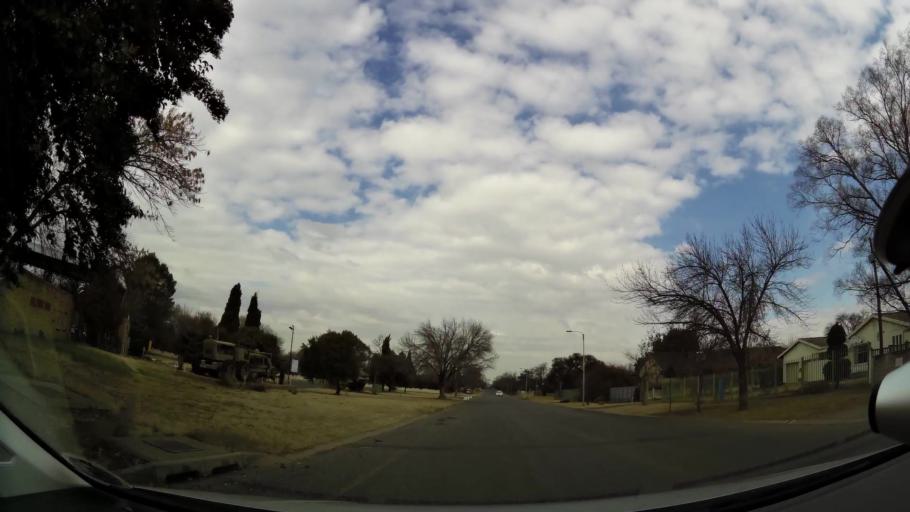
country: ZA
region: Orange Free State
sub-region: Fezile Dabi District Municipality
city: Kroonstad
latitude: -27.6433
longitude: 27.2387
